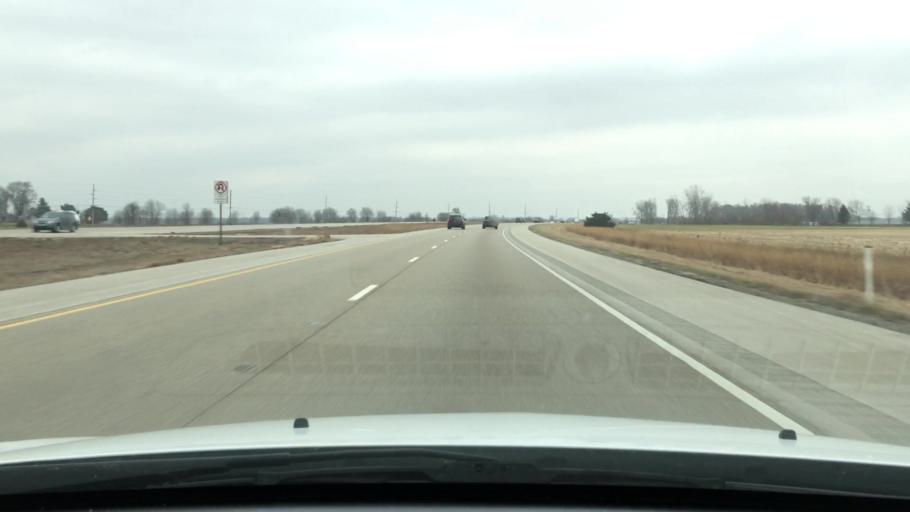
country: US
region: Illinois
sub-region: Logan County
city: Lincoln
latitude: 40.1950
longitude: -89.3050
